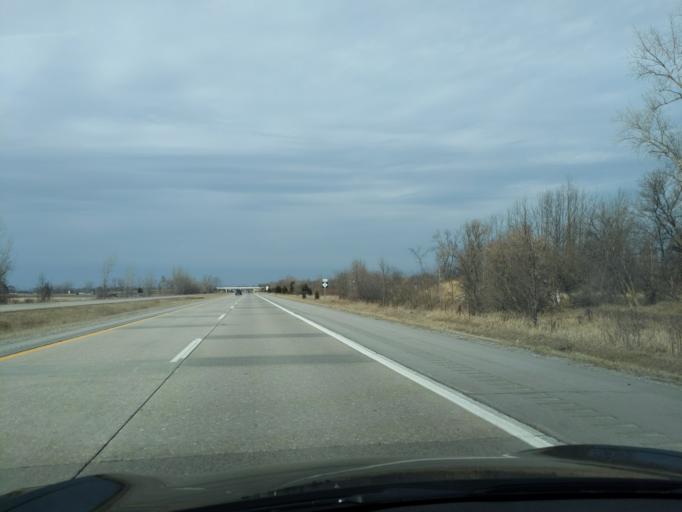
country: US
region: Michigan
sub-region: Bay County
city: Bay City
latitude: 43.6318
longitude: -83.9417
